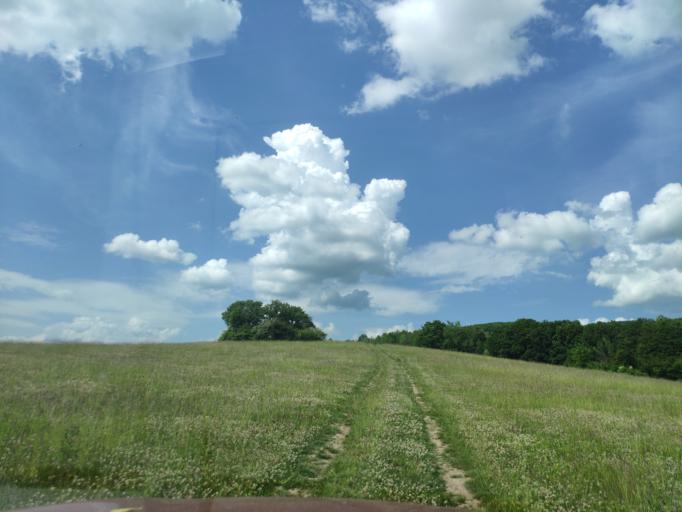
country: SK
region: Kosicky
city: Medzev
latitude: 48.7172
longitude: 20.9626
